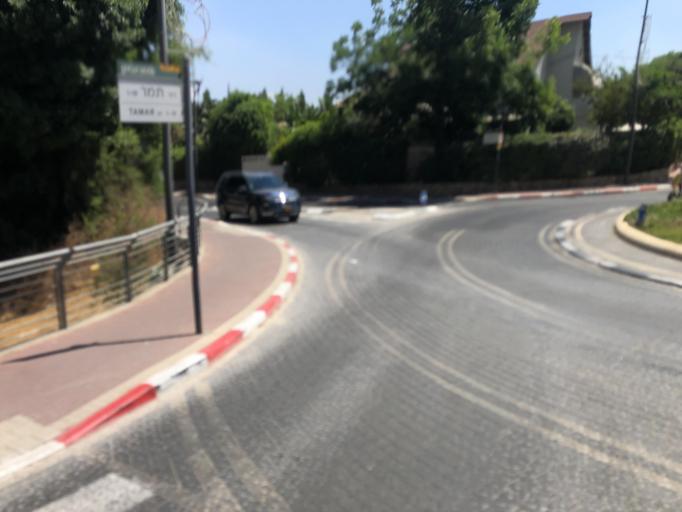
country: IL
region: Tel Aviv
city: Or Yehuda
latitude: 32.0255
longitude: 34.8749
